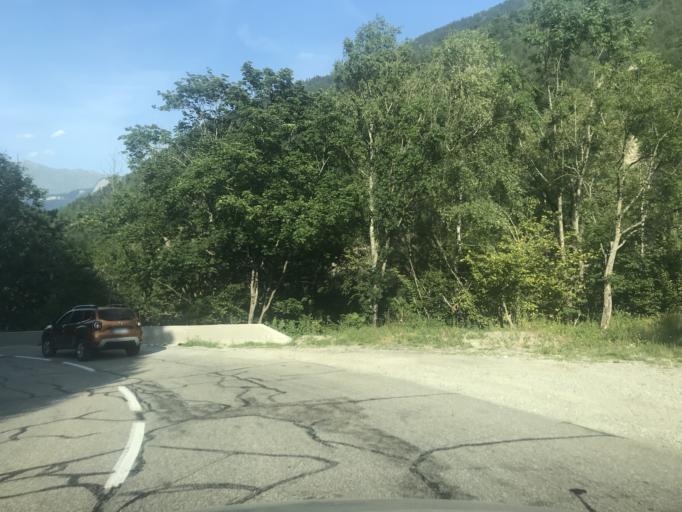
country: FR
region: Rhone-Alpes
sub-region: Departement de la Savoie
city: Saint-Etienne-de-Cuines
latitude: 45.3105
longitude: 6.2615
